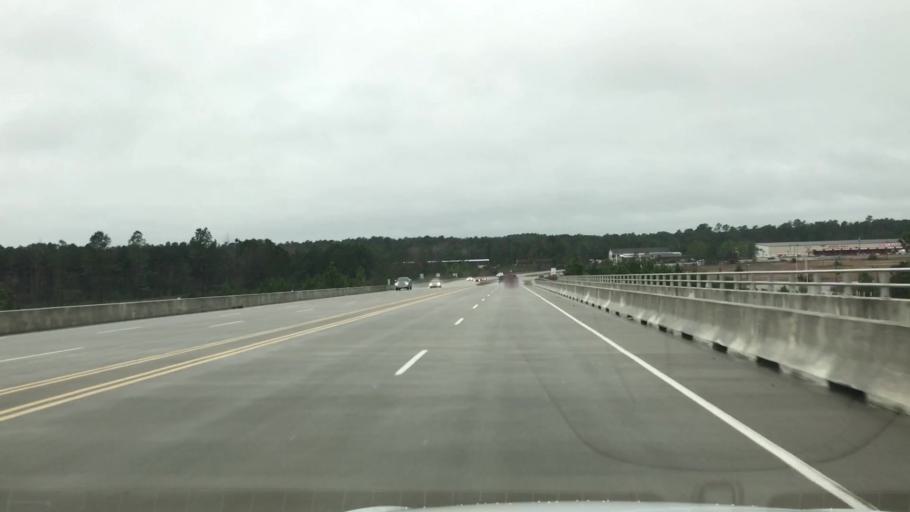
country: US
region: South Carolina
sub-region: Horry County
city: Forestbrook
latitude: 33.7065
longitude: -78.9362
